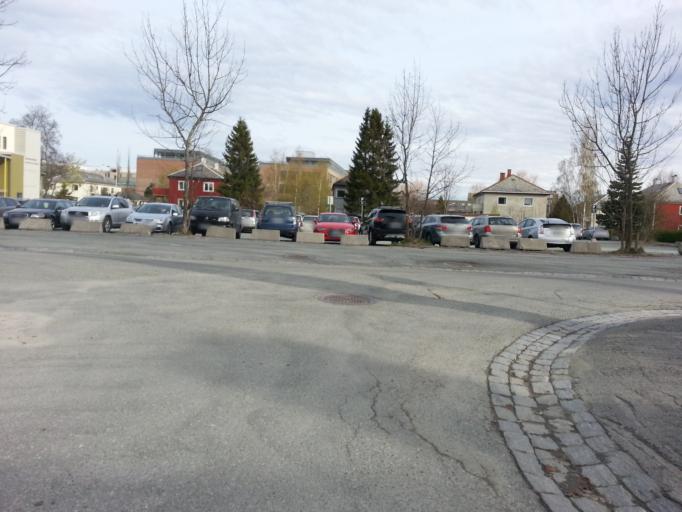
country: NO
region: Sor-Trondelag
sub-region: Trondheim
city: Trondheim
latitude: 63.4173
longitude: 10.3935
